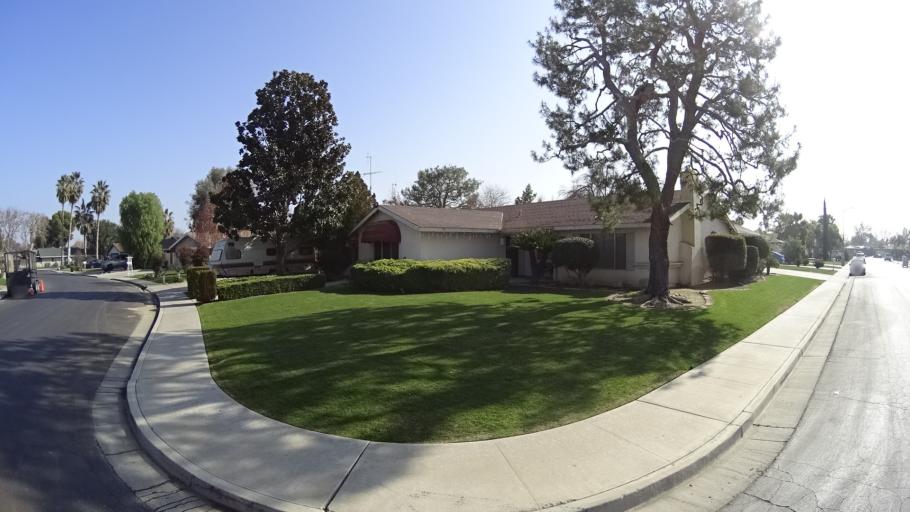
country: US
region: California
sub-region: Kern County
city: Greenacres
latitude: 35.3241
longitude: -119.0730
